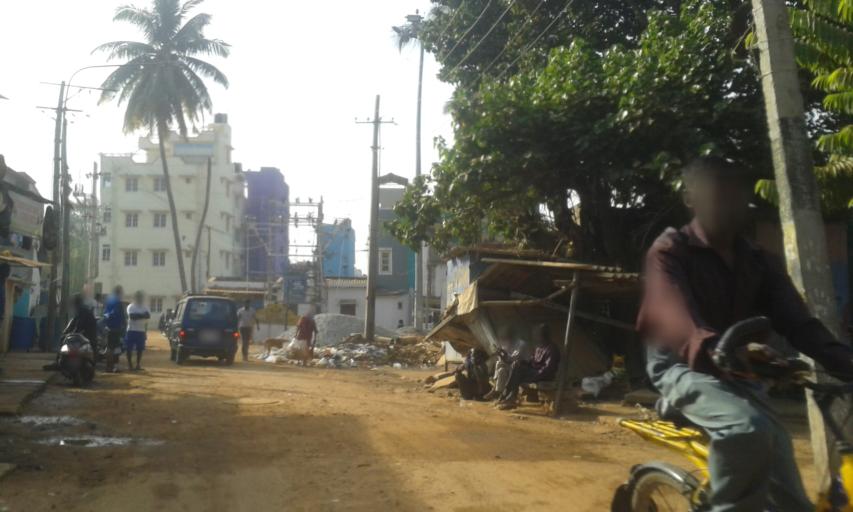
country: IN
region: Karnataka
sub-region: Bangalore Urban
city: Bangalore
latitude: 12.9616
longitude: 77.6179
